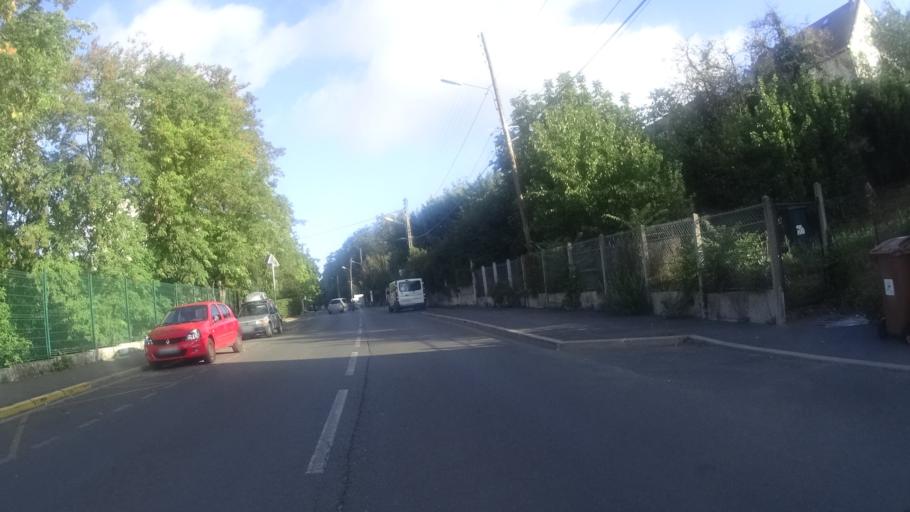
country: FR
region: Ile-de-France
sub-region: Departement de l'Essonne
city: Draveil
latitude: 48.6753
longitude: 2.4074
